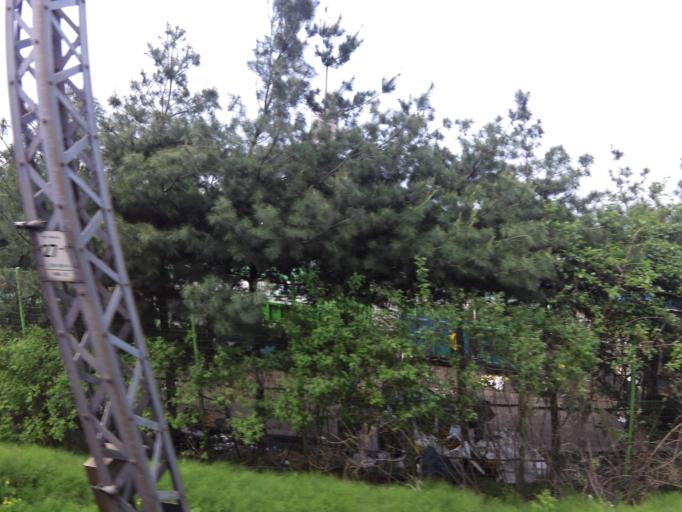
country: KR
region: Seoul
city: Seoul
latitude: 37.5156
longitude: 126.9469
